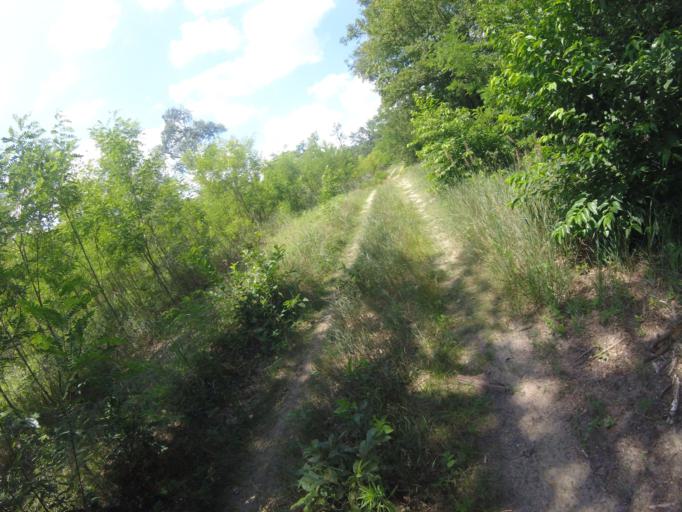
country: HU
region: Pest
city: Nagykoros
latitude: 47.0706
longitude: 19.7298
